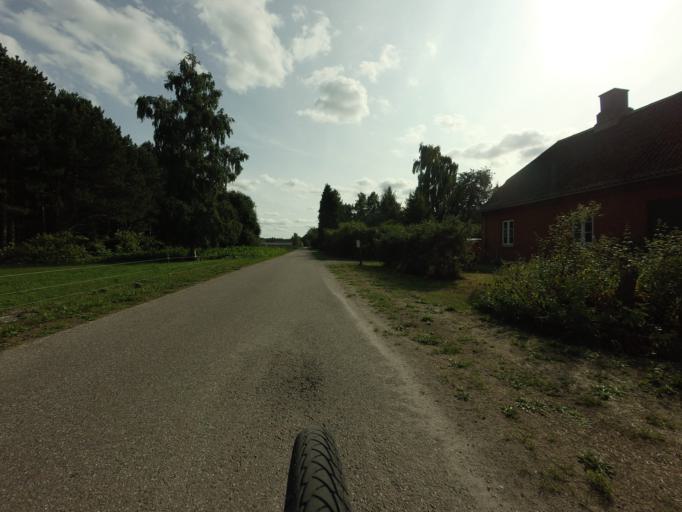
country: DK
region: Zealand
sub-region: Vordingborg Kommune
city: Praesto
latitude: 55.1631
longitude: 12.0931
